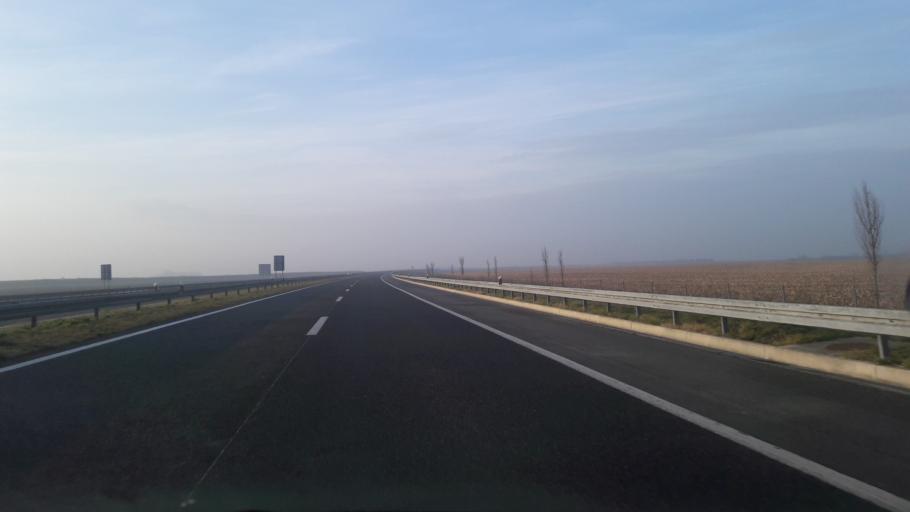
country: HR
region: Osjecko-Baranjska
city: Cepin
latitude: 45.5566
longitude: 18.5423
